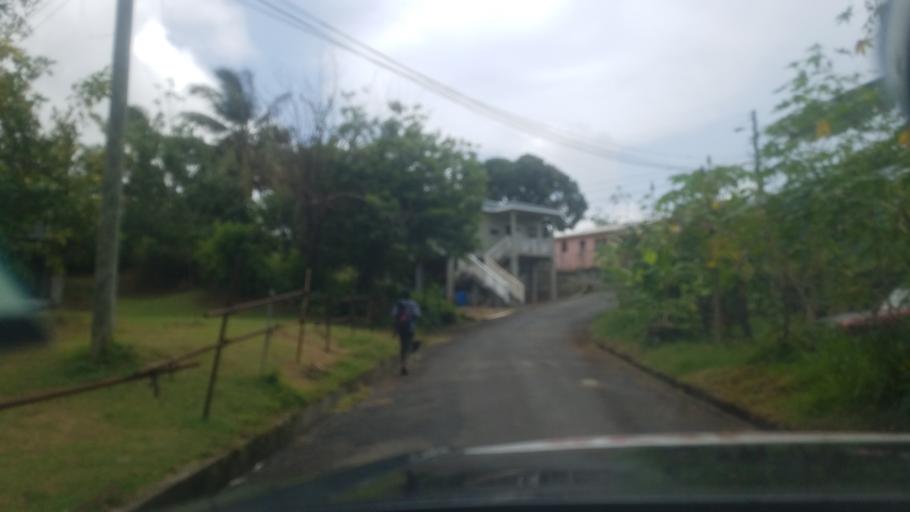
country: LC
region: Laborie Quarter
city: Laborie
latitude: 13.7464
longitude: -60.9630
